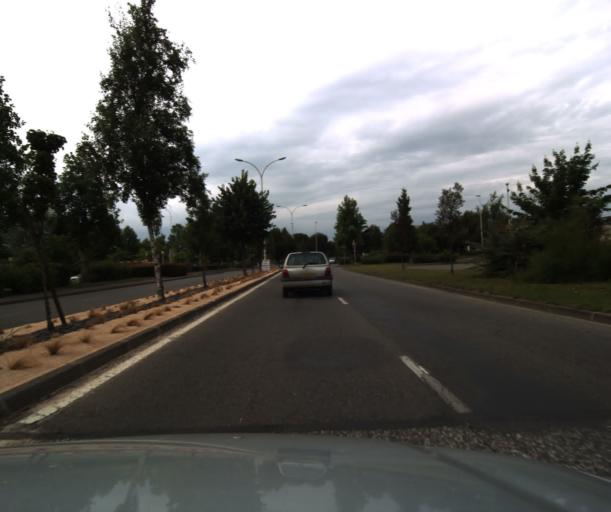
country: FR
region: Midi-Pyrenees
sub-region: Departement des Hautes-Pyrenees
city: Tarbes
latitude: 43.2241
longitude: 0.0909
